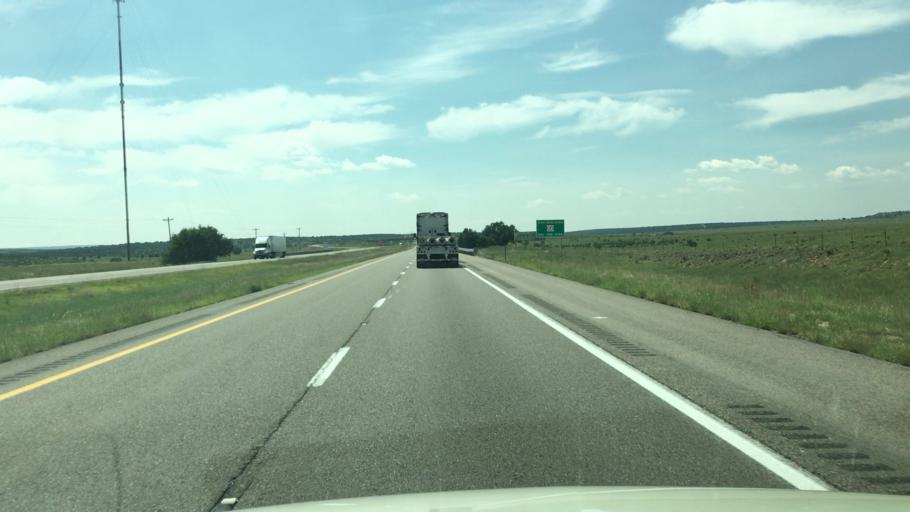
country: US
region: New Mexico
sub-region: Guadalupe County
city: Santa Rosa
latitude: 34.9912
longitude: -105.2848
